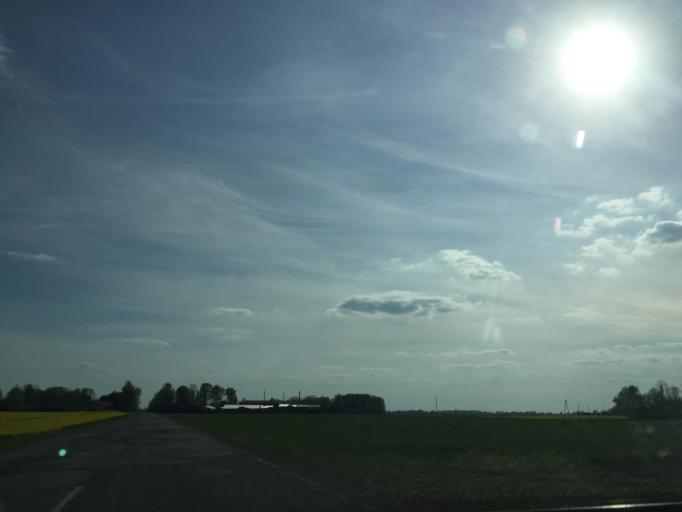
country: LV
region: Bauskas Rajons
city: Bauska
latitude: 56.4446
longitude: 24.2474
